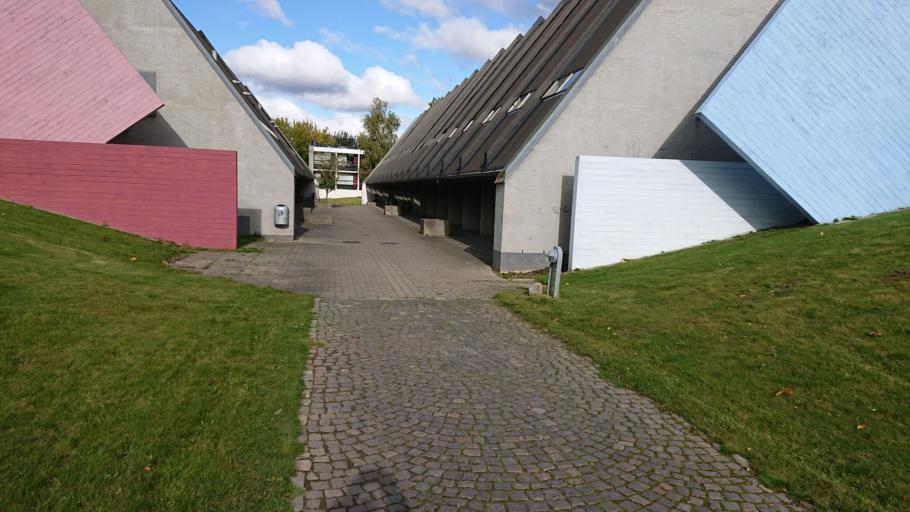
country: DK
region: Central Jutland
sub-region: Arhus Kommune
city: Stavtrup
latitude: 56.1696
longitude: 10.1163
